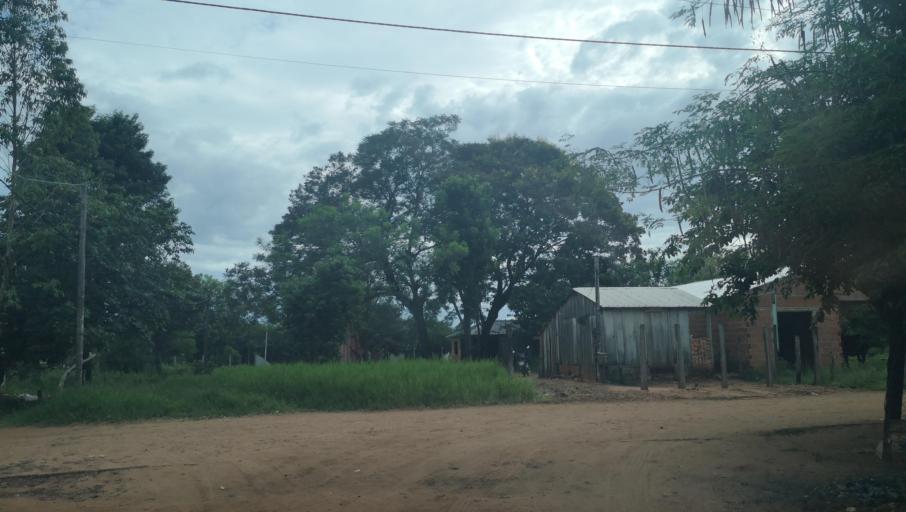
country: PY
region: San Pedro
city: Capiibary
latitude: -24.7329
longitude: -56.0236
